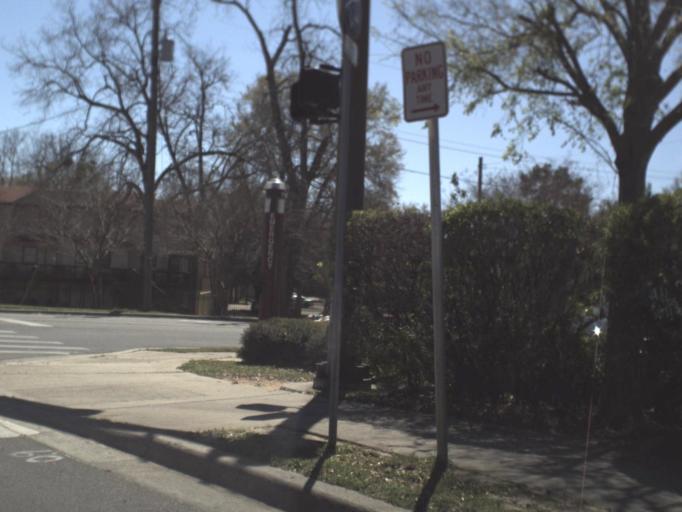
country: US
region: Florida
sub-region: Leon County
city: Tallahassee
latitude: 30.4363
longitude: -84.3059
